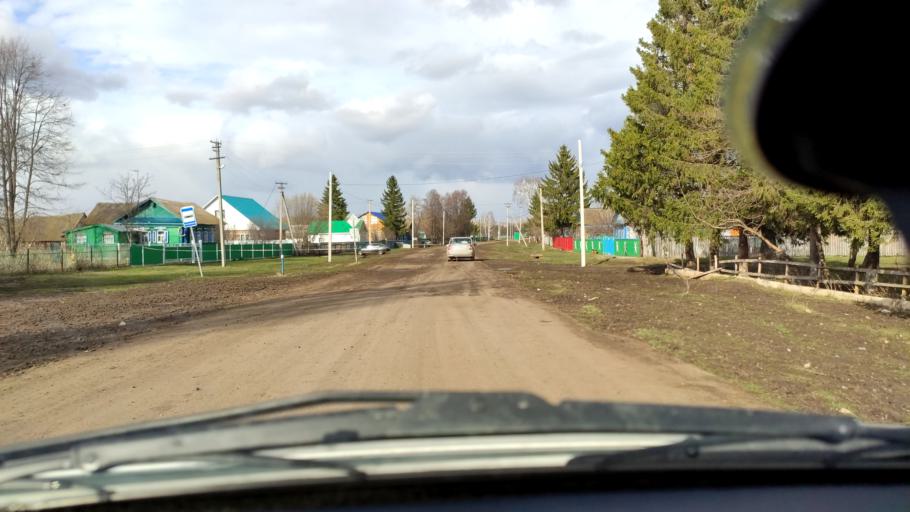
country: RU
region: Bashkortostan
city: Buzdyak
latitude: 54.7649
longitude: 54.6181
